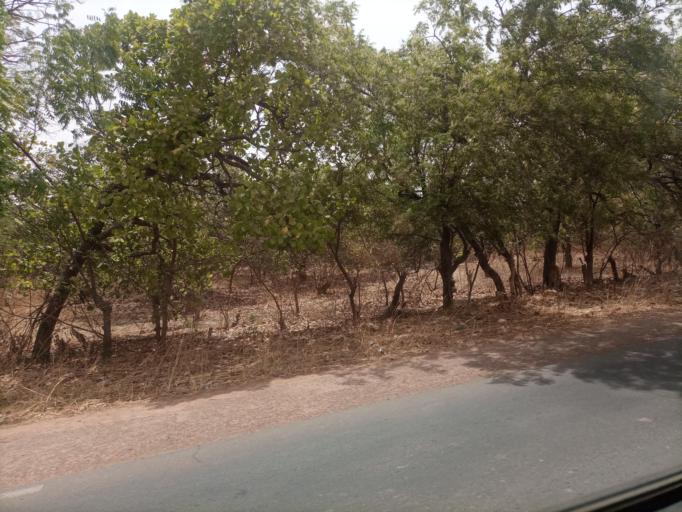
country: SN
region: Fatick
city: Sokone
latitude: 13.7078
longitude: -16.4286
